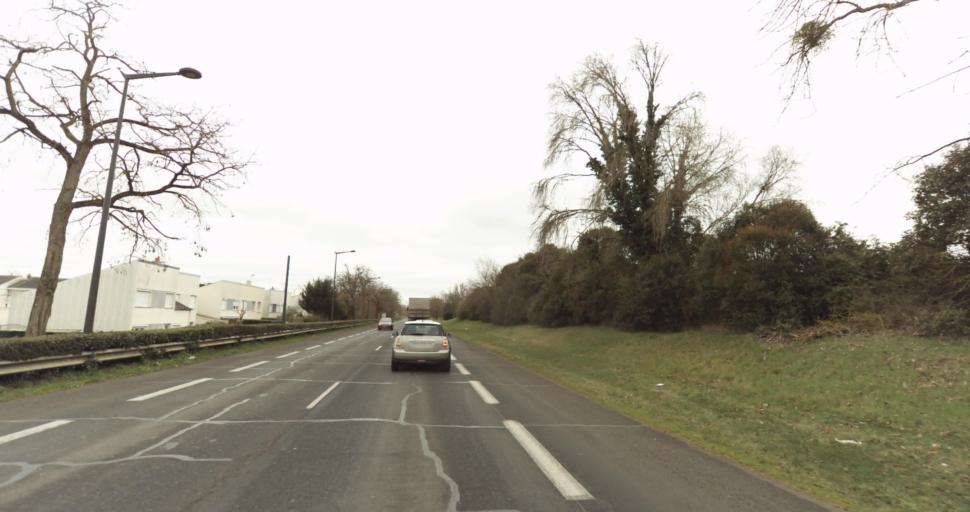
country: FR
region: Pays de la Loire
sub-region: Departement de Maine-et-Loire
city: Saumur
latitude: 47.2450
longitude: -0.0793
